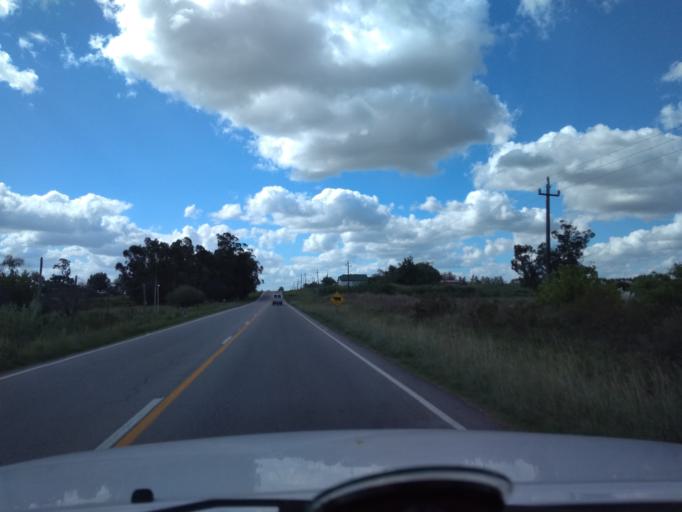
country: UY
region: Canelones
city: Joaquin Suarez
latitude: -34.6981
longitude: -56.0564
